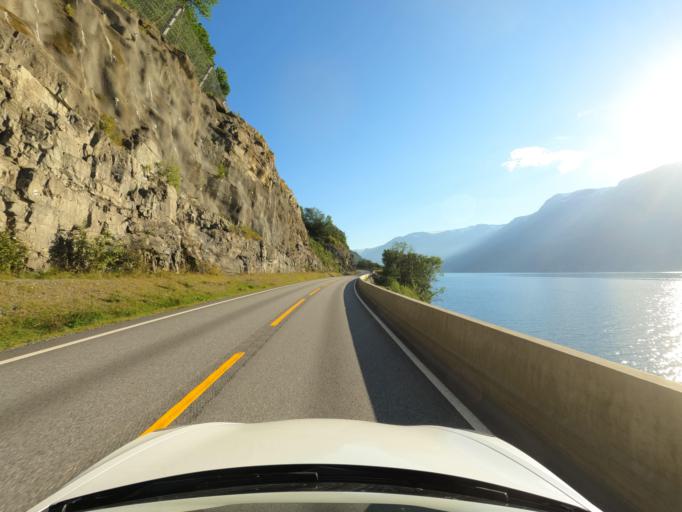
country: NO
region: Hordaland
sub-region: Ullensvang
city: Kinsarvik
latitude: 60.3044
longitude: 6.6439
